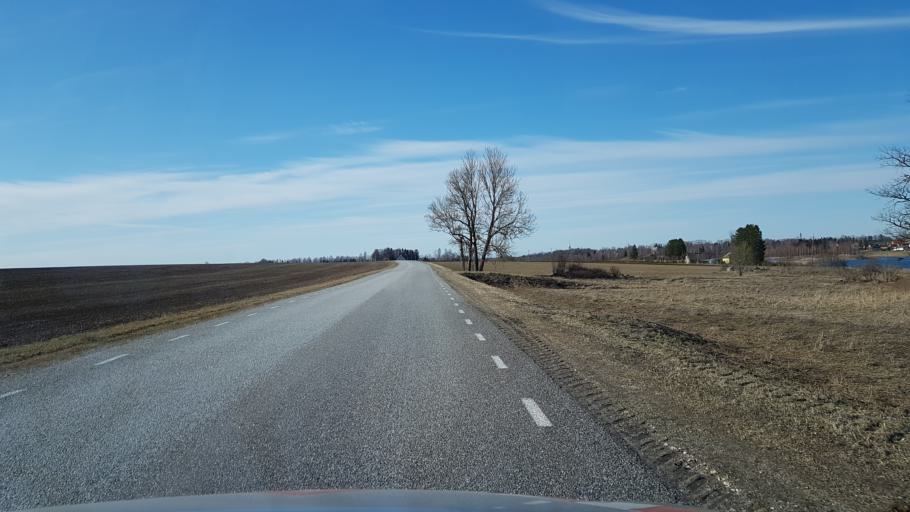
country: EE
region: Laeaene-Virumaa
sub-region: Kadrina vald
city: Kadrina
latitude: 59.3263
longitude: 26.1393
